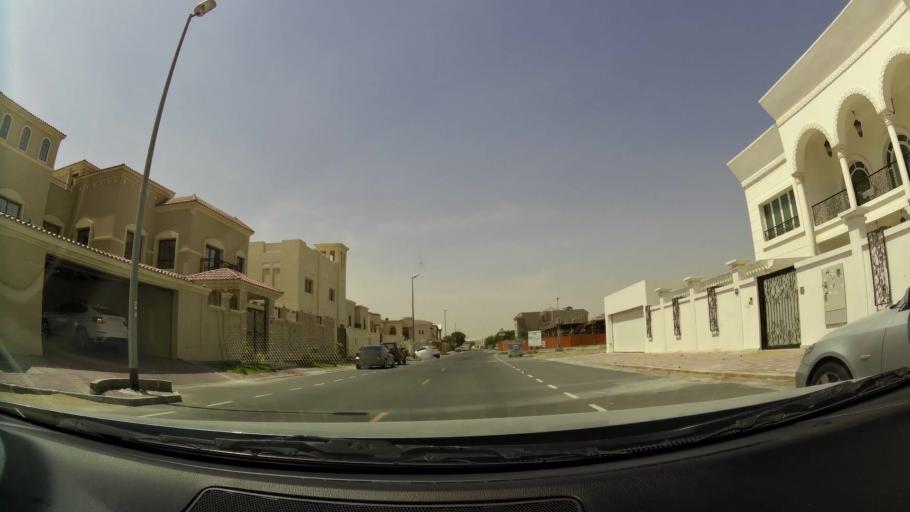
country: AE
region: Ash Shariqah
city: Sharjah
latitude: 25.1825
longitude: 55.4261
